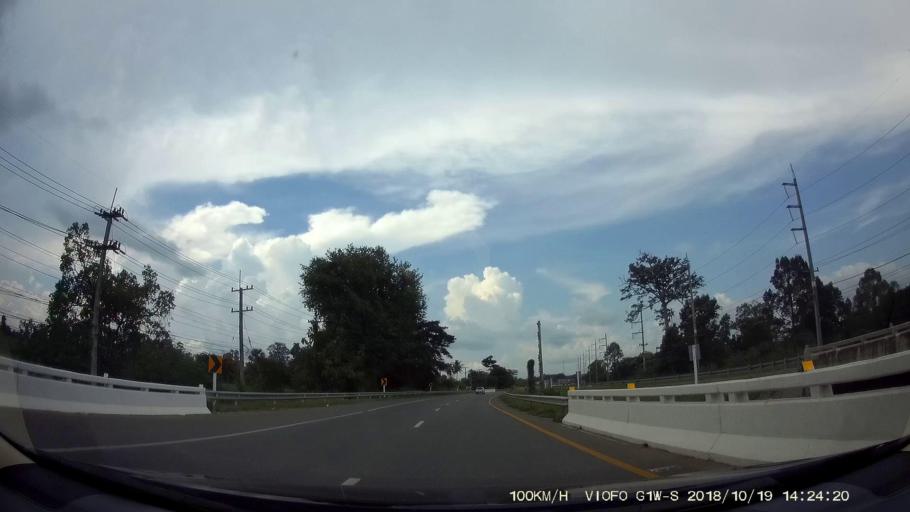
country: TH
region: Chaiyaphum
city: Kaeng Khro
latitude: 16.0796
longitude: 102.2736
